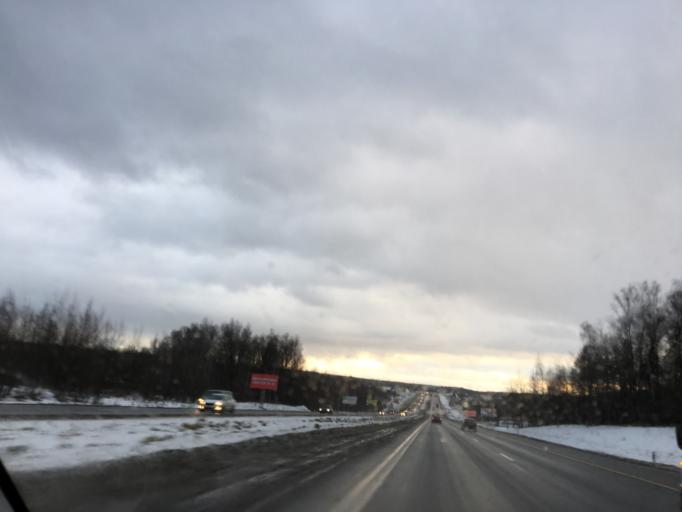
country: RU
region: Moskovskaya
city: Danki
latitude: 54.9548
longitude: 37.5295
